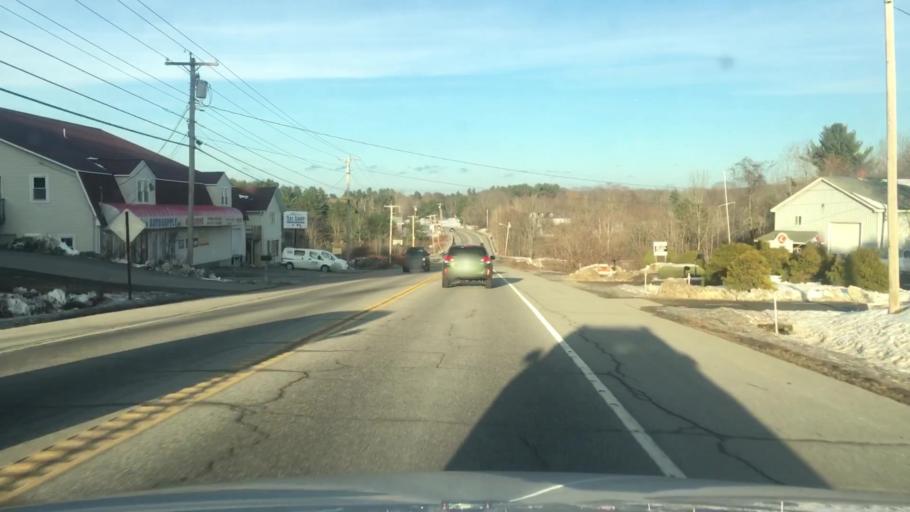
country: US
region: Maine
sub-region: Kennebec County
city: Hallowell
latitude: 44.2903
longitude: -69.7725
